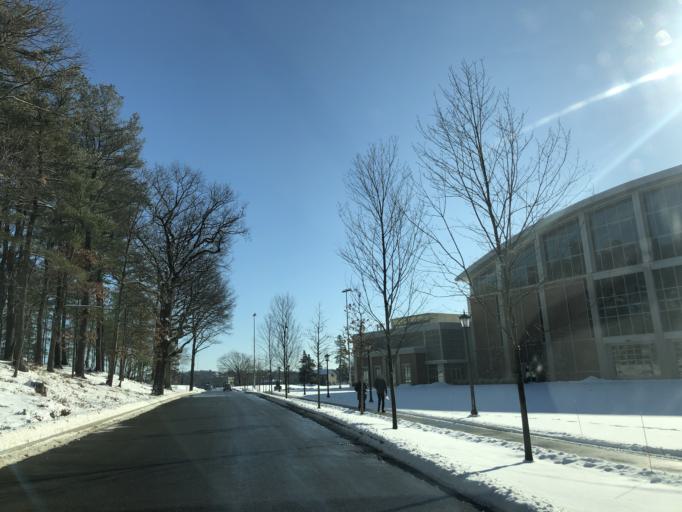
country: US
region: Massachusetts
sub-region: Middlesex County
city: Watertown
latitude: 42.3357
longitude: -71.1652
